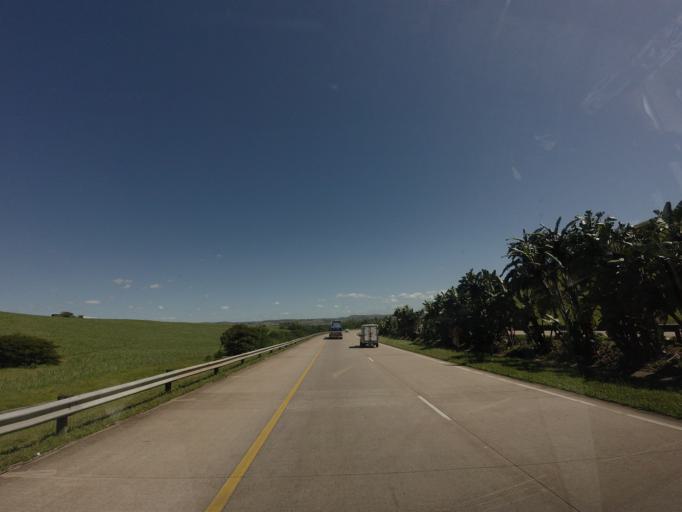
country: ZA
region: KwaZulu-Natal
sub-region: iLembe District Municipality
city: Stanger
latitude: -29.3841
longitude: 31.2971
